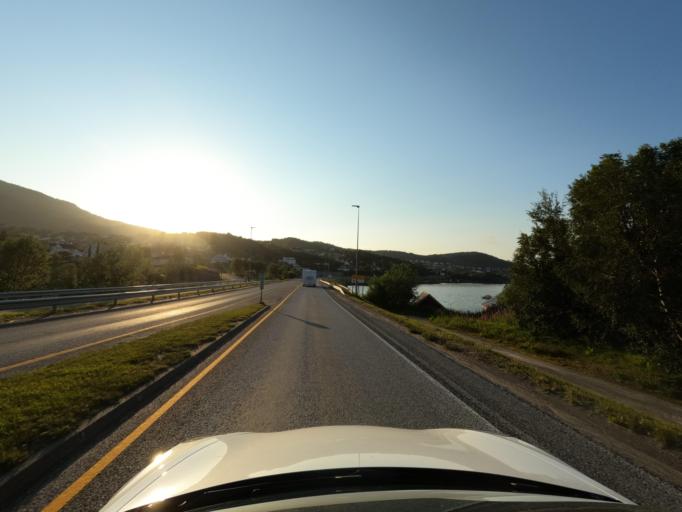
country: NO
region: Troms
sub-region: Harstad
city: Harstad
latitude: 68.7608
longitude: 16.5649
